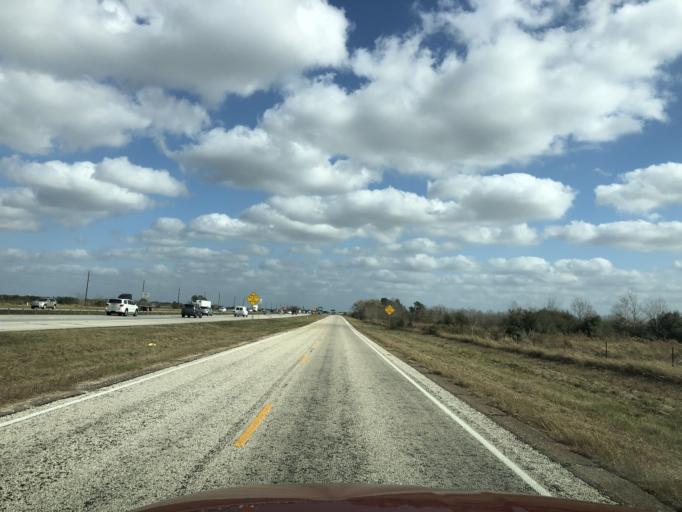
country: US
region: Texas
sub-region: Austin County
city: Sealy
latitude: 29.7602
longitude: -96.2098
